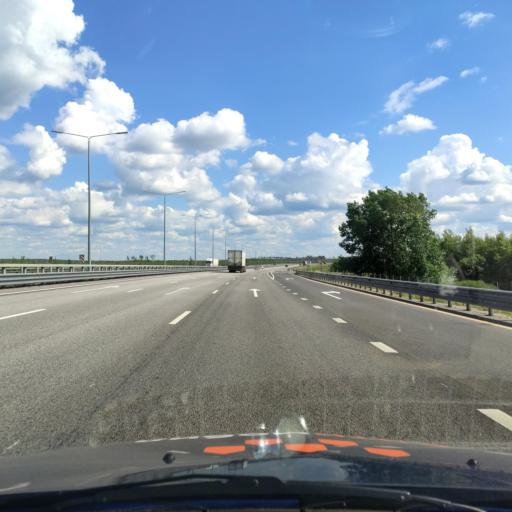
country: RU
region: Voronezj
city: Somovo
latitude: 51.7786
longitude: 39.2952
